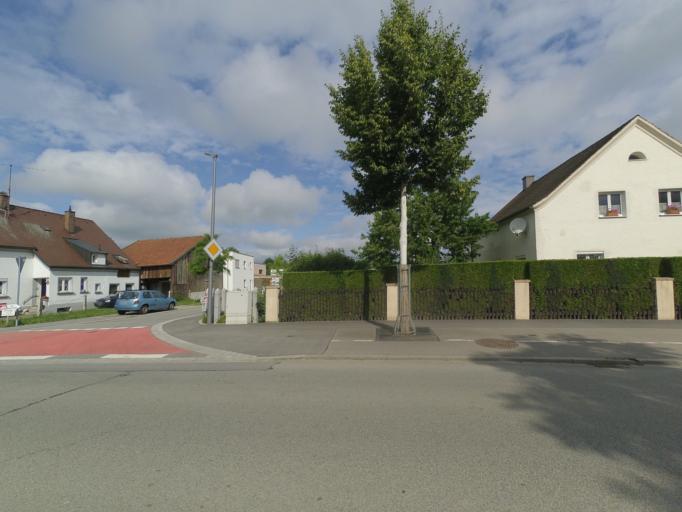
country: DE
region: Bavaria
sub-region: Lower Bavaria
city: Straubing
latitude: 48.8890
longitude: 12.5754
